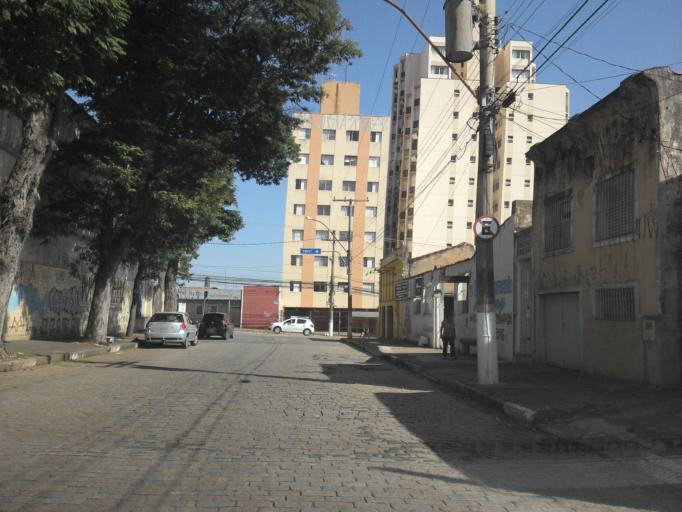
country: BR
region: Sao Paulo
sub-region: Campinas
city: Campinas
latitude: -22.9108
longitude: -47.0659
